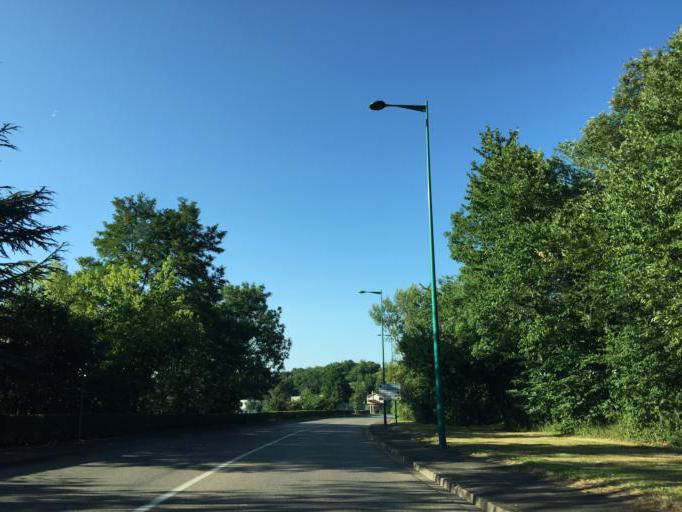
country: FR
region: Rhone-Alpes
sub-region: Departement de la Loire
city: La Talaudiere
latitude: 45.4644
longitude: 4.4280
